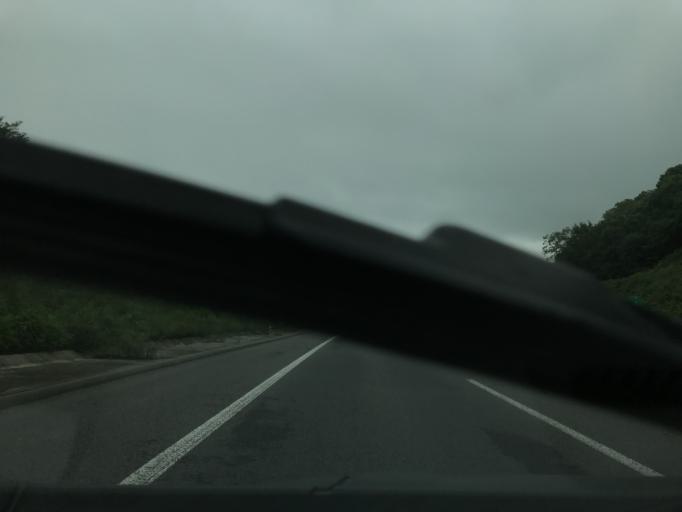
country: JP
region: Oita
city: Bungo-Takada-shi
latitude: 33.5033
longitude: 131.3108
